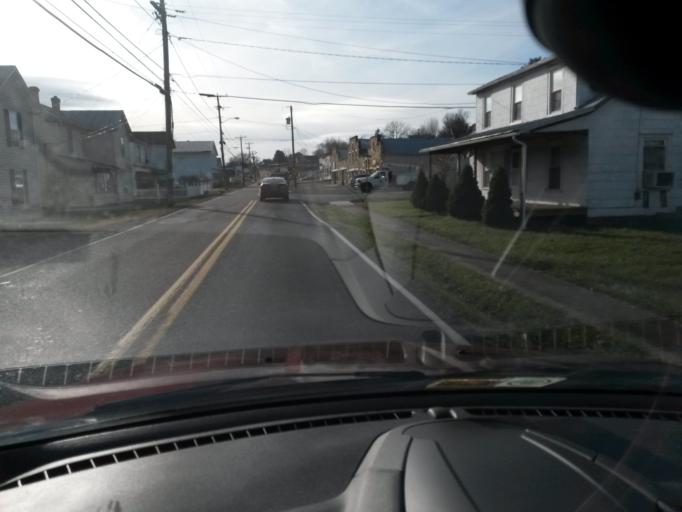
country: US
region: Virginia
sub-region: Rockbridge County
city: East Lexington
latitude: 38.0789
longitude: -79.3830
